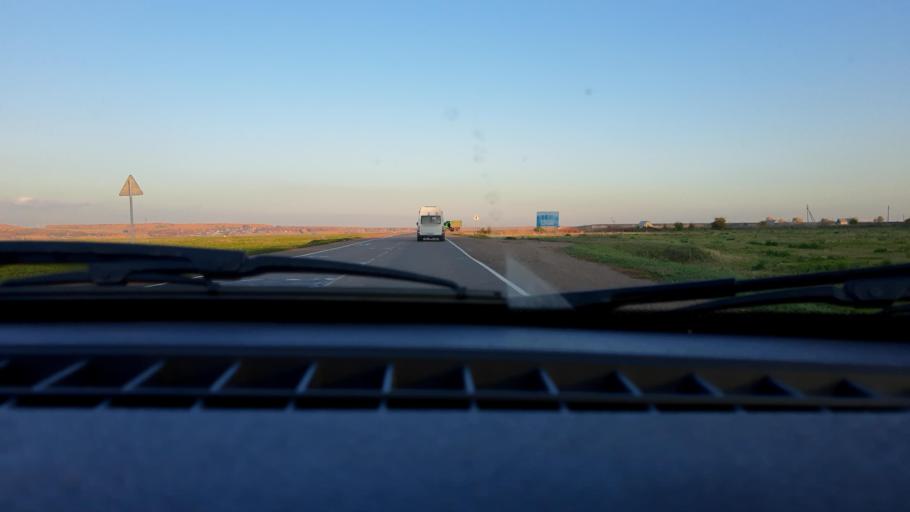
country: RU
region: Bashkortostan
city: Asanovo
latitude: 54.8258
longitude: 55.6429
